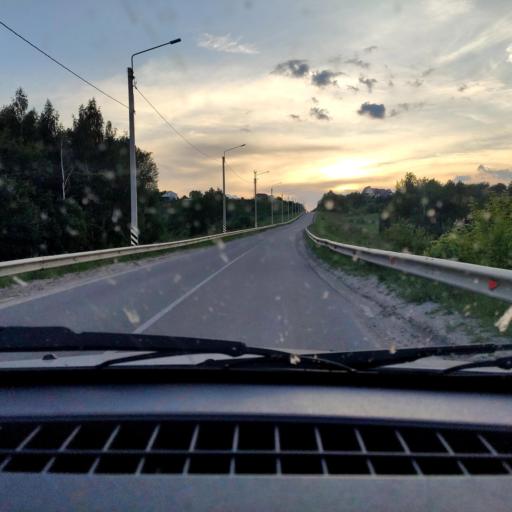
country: RU
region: Voronezj
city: Ramon'
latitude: 51.9492
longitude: 39.3746
